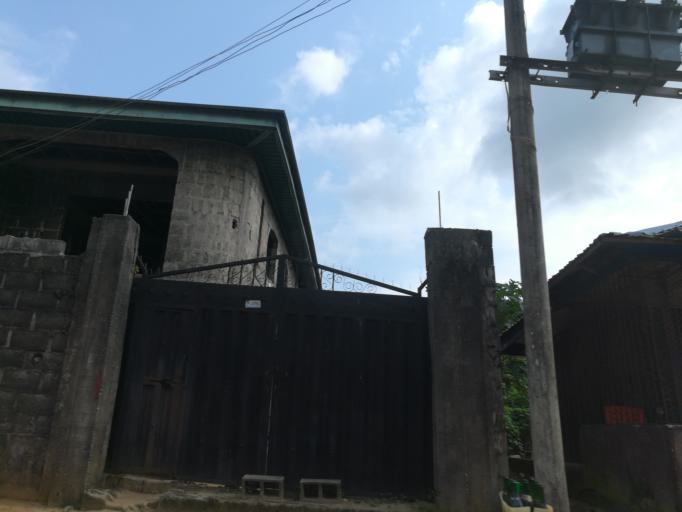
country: NG
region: Rivers
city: Okrika
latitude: 4.7447
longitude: 7.1130
